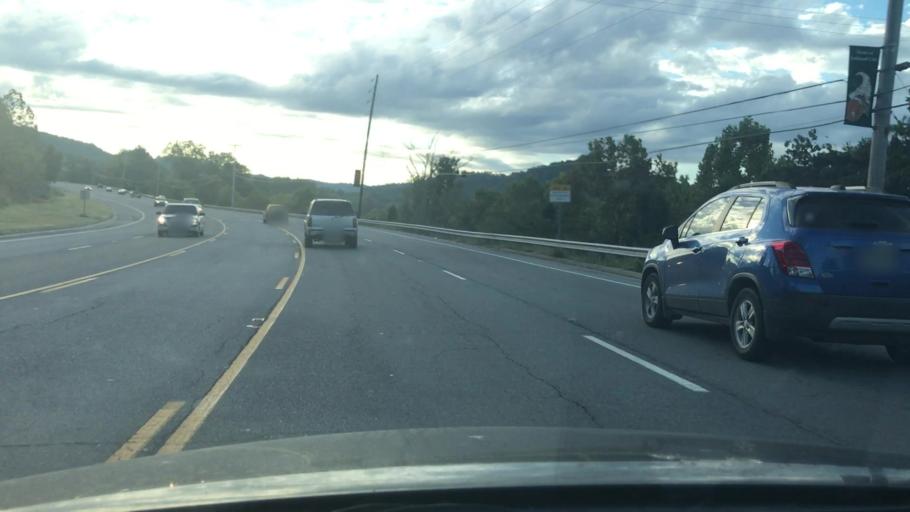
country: US
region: Tennessee
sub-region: Cheatham County
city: Ashland City
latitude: 36.2632
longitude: -87.0575
